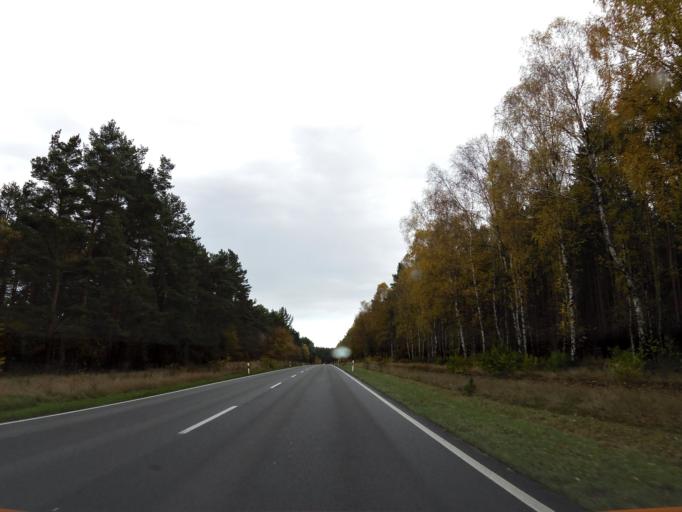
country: DE
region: Saxony-Anhalt
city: Haldensleben I
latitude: 52.3634
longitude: 11.4533
